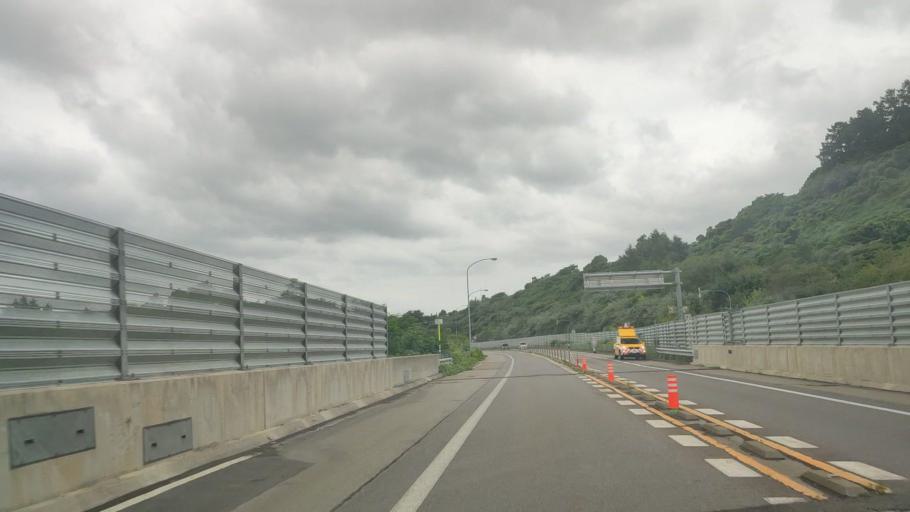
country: JP
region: Hokkaido
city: Nanae
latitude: 41.9130
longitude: 140.6913
